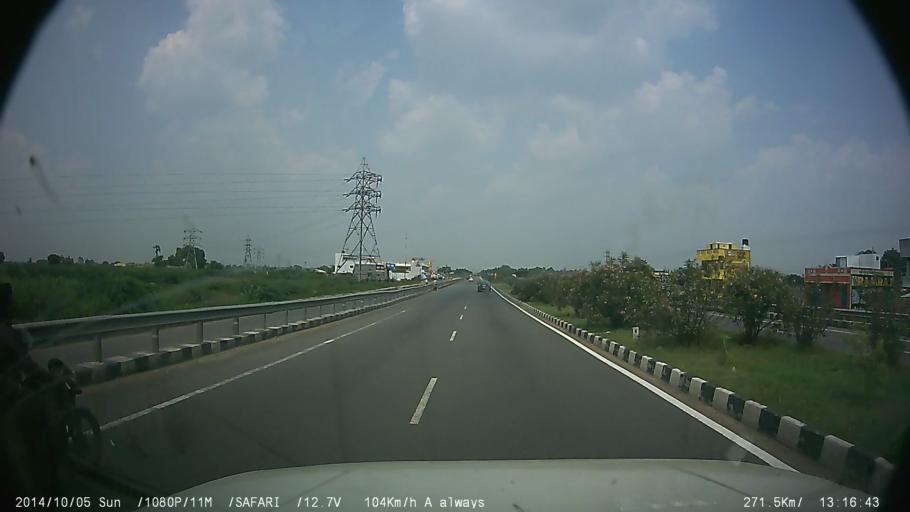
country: IN
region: Tamil Nadu
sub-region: Villupuram
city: Vikravandi
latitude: 12.0058
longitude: 79.5248
